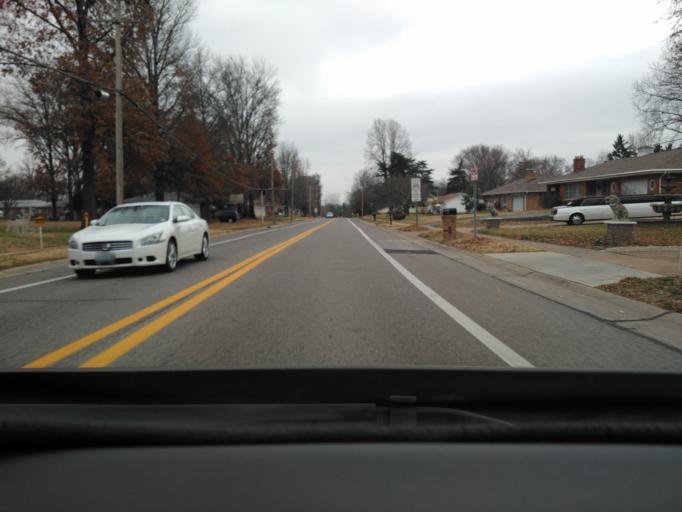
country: US
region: Missouri
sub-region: Saint Louis County
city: Concord
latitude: 38.4999
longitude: -90.3591
